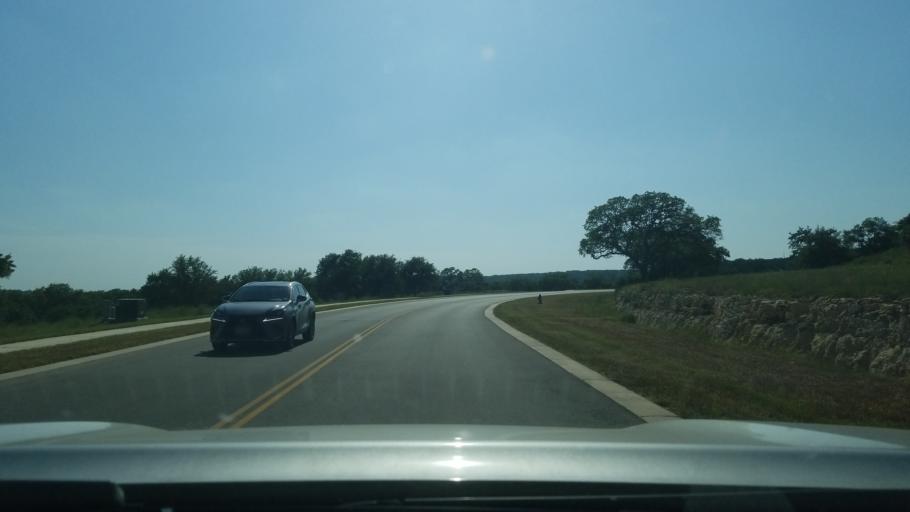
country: US
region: Texas
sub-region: Comal County
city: Bulverde
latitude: 29.7614
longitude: -98.4242
